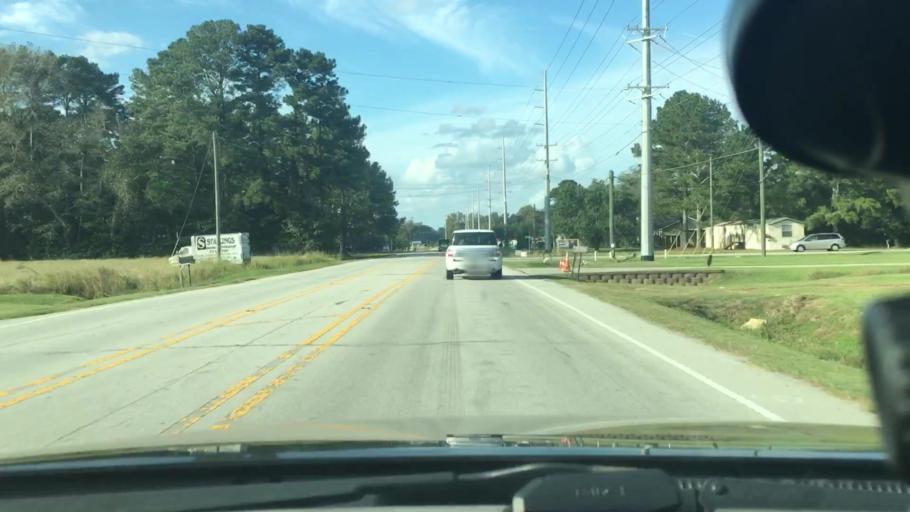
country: US
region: North Carolina
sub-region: Pitt County
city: Windsor
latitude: 35.5433
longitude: -77.3230
